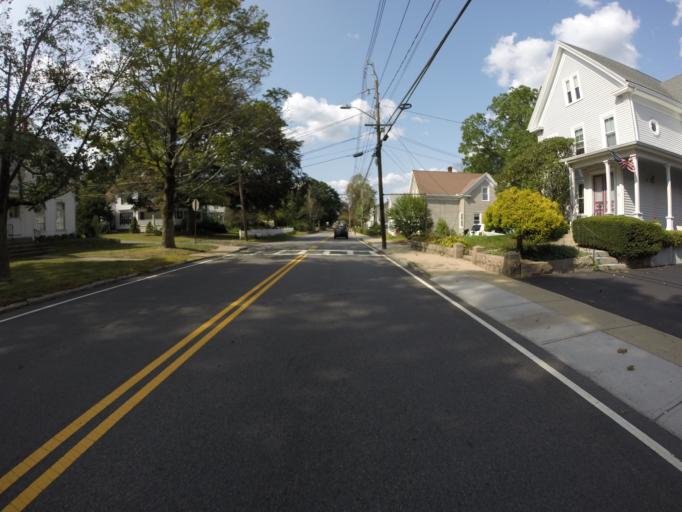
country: US
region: Massachusetts
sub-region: Bristol County
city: Easton
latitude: 42.0633
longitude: -71.1026
